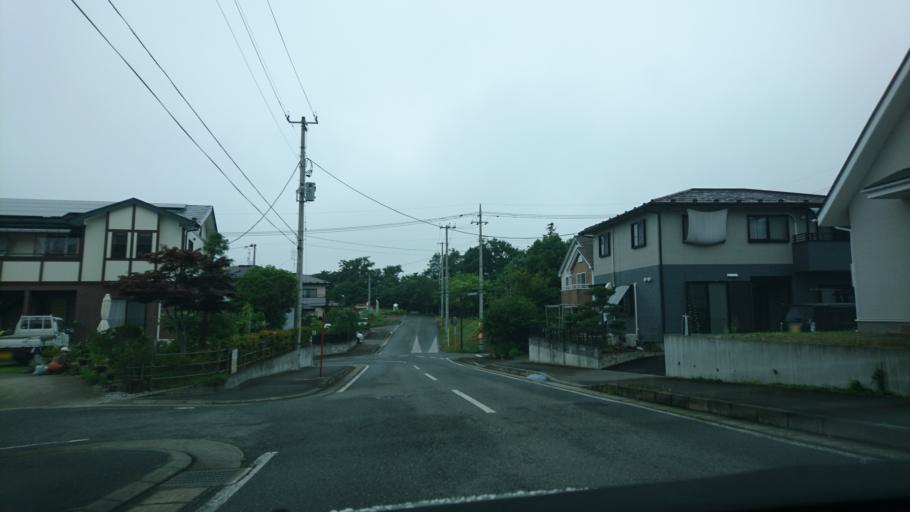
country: JP
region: Iwate
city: Ichinoseki
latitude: 38.9194
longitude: 141.1505
